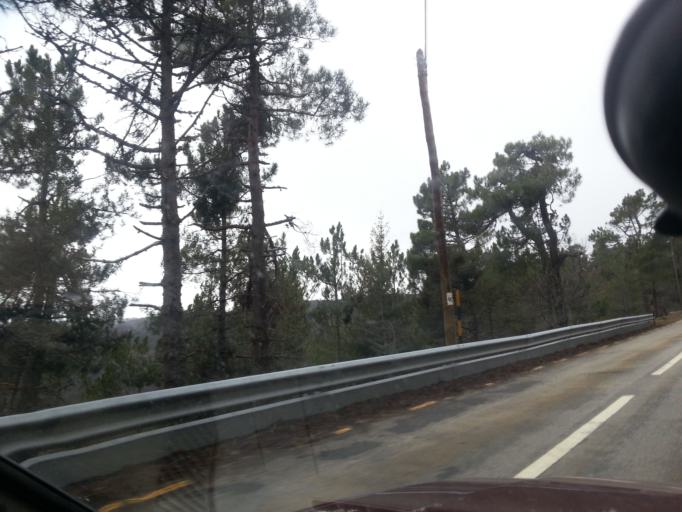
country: PT
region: Guarda
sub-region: Manteigas
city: Manteigas
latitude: 40.4171
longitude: -7.5434
